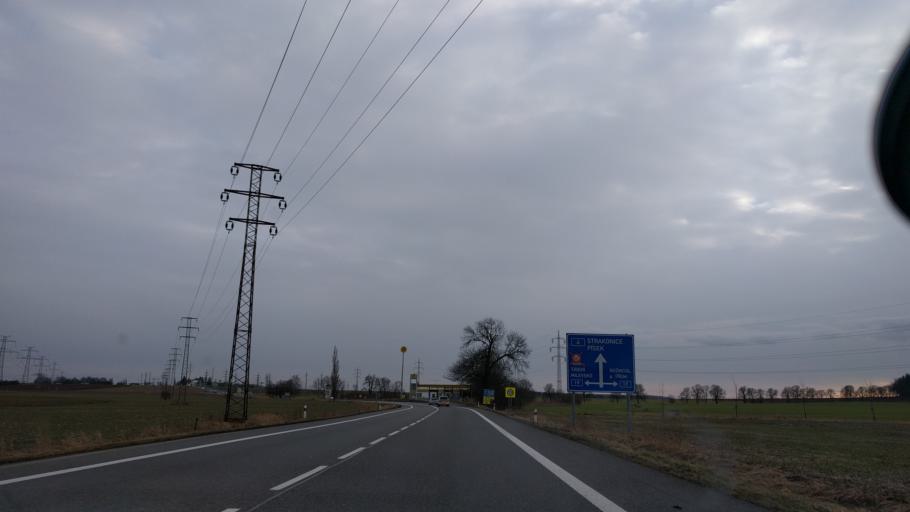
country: CZ
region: Jihocesky
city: Mirovice
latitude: 49.5257
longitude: 14.0738
